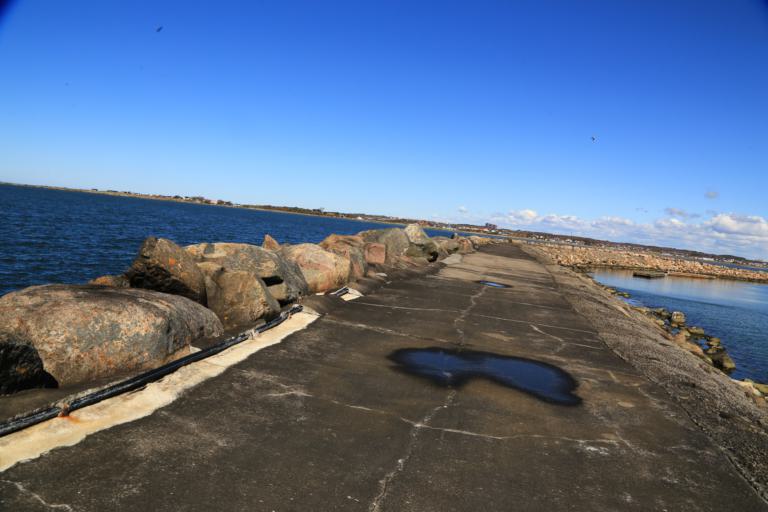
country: SE
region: Halland
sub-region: Varbergs Kommun
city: Traslovslage
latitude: 57.0580
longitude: 12.2672
